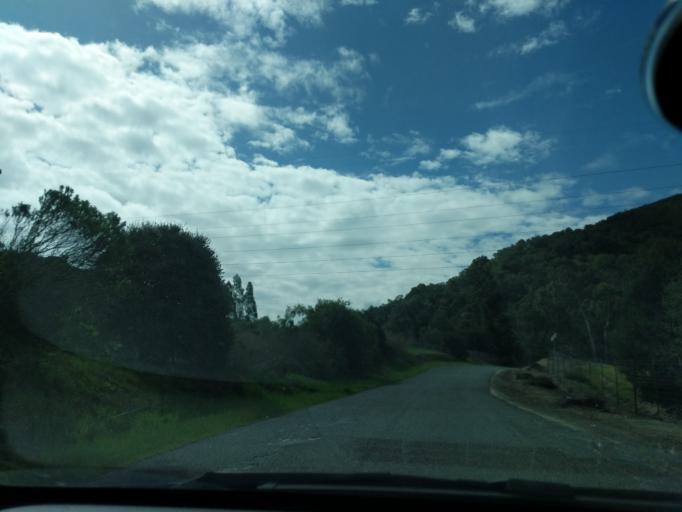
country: US
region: California
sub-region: Monterey County
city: Prunedale
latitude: 36.7745
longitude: -121.5885
